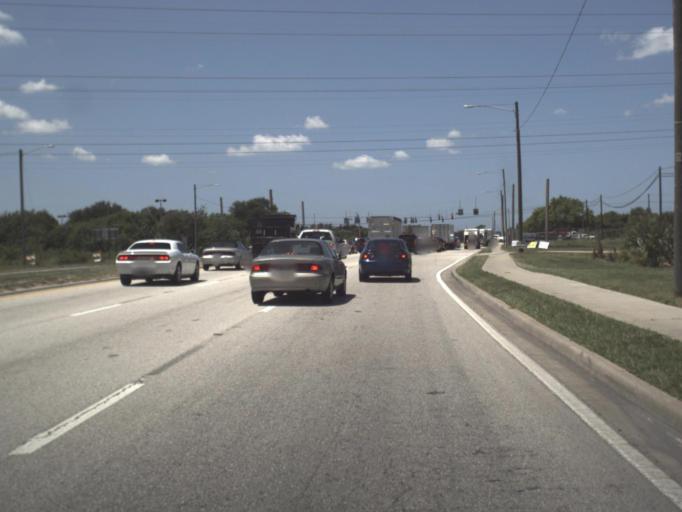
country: US
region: Florida
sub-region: Pinellas County
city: Pinellas Park
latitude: 27.8792
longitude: -82.6980
